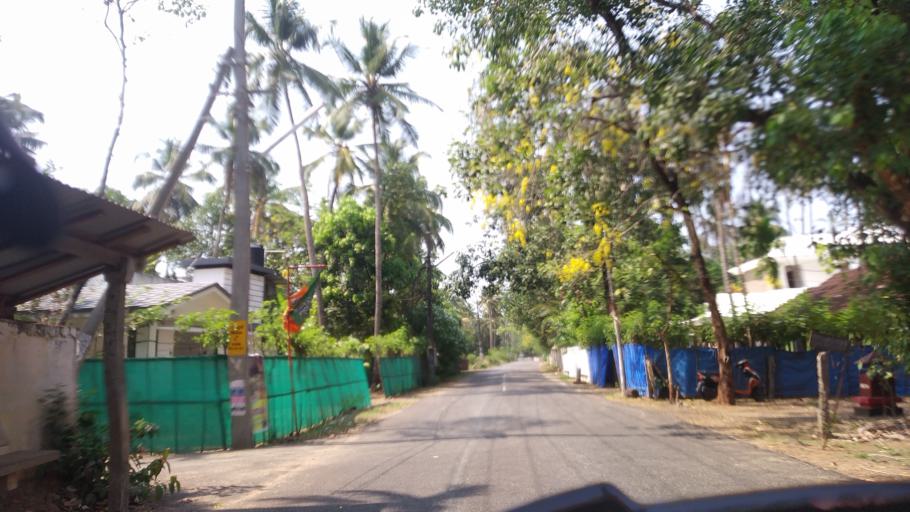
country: IN
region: Kerala
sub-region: Thrissur District
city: Thanniyam
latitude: 10.3657
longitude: 76.1068
